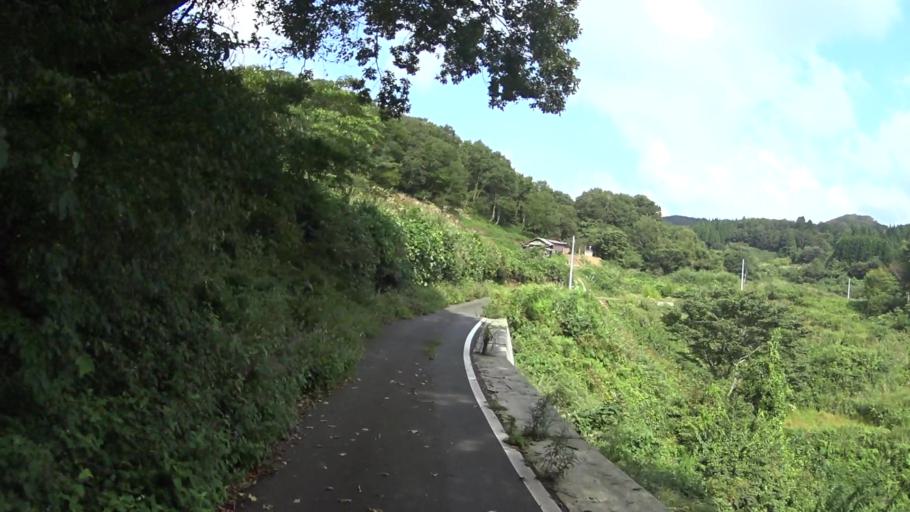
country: JP
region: Kyoto
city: Miyazu
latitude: 35.6396
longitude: 135.1815
